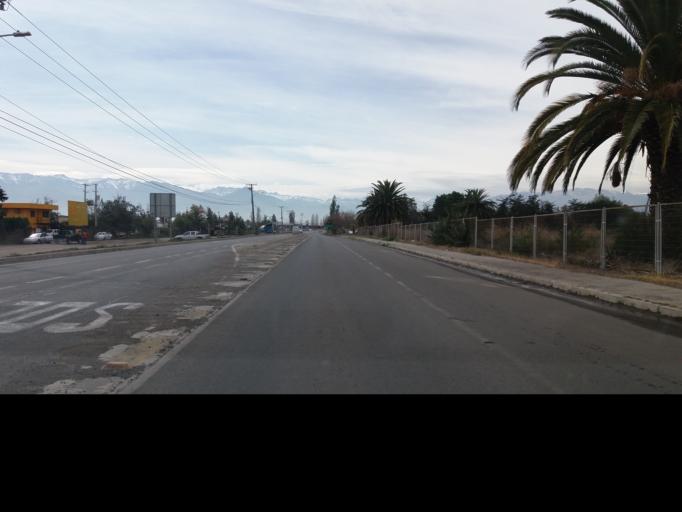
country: CL
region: Valparaiso
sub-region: Provincia de San Felipe
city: San Felipe
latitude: -32.7729
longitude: -70.7150
